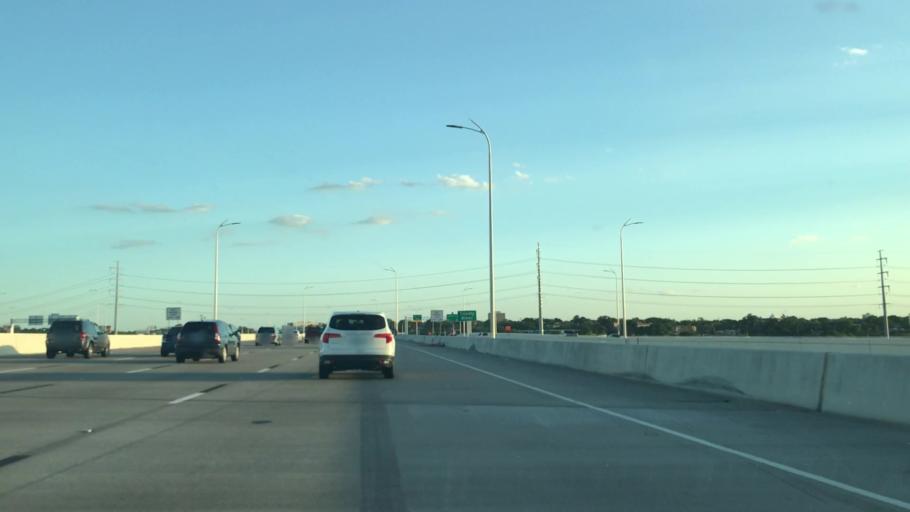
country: US
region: Texas
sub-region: Dallas County
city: Dallas
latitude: 32.7645
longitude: -96.8068
